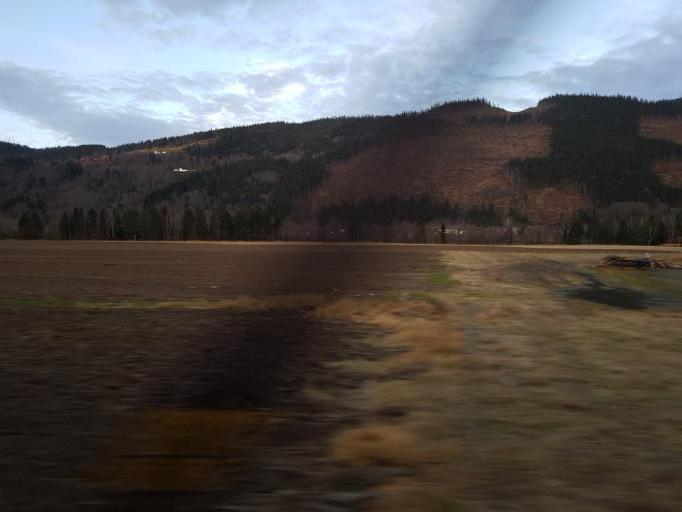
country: NO
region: Sor-Trondelag
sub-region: Melhus
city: Lundamo
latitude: 63.1360
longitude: 10.2527
